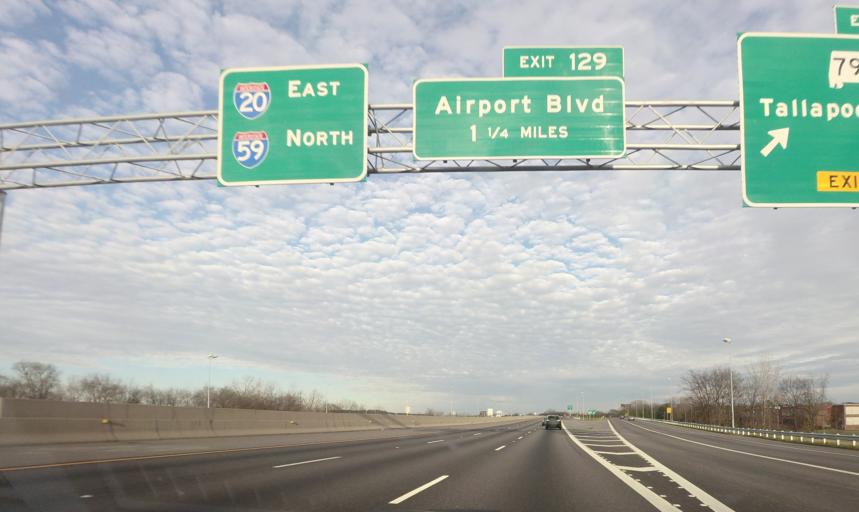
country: US
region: Alabama
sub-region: Jefferson County
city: Birmingham
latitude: 33.5466
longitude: -86.7827
